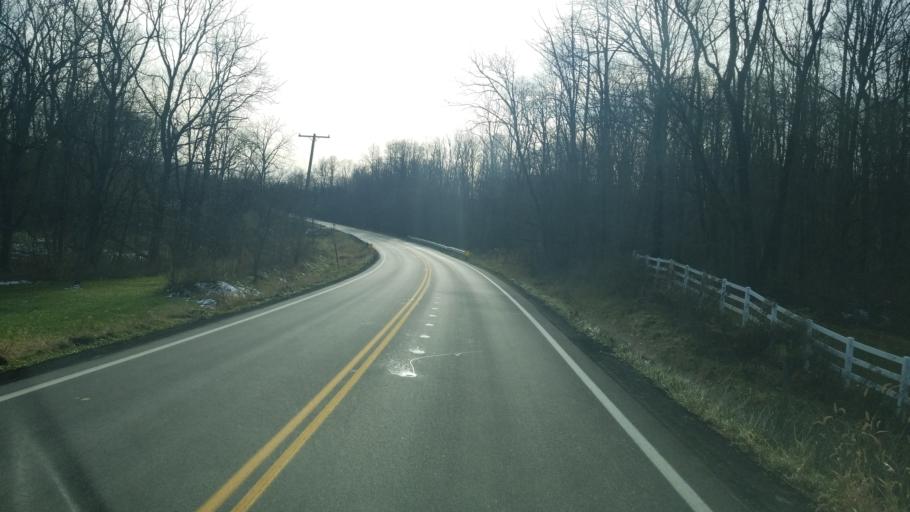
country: US
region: Ohio
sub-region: Ashland County
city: Ashland
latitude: 40.9521
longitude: -82.2623
